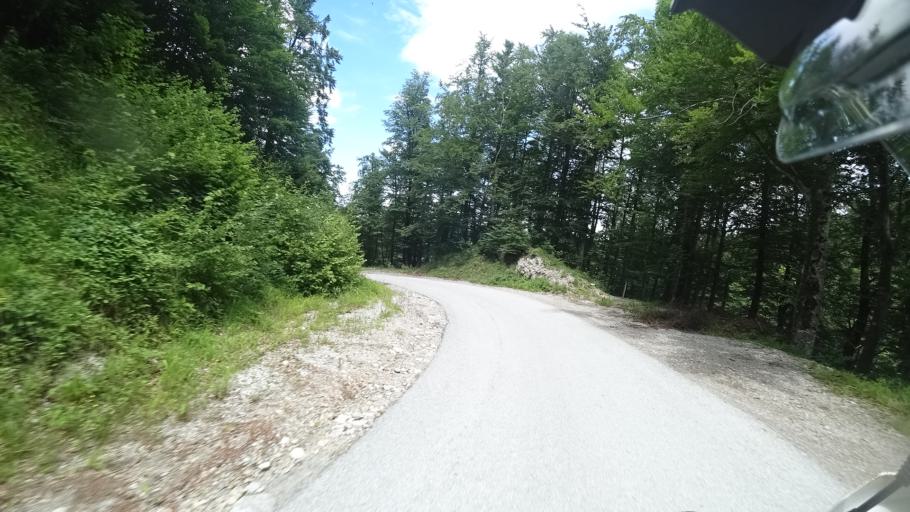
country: SI
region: Osilnica
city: Osilnica
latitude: 45.4981
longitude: 14.6276
